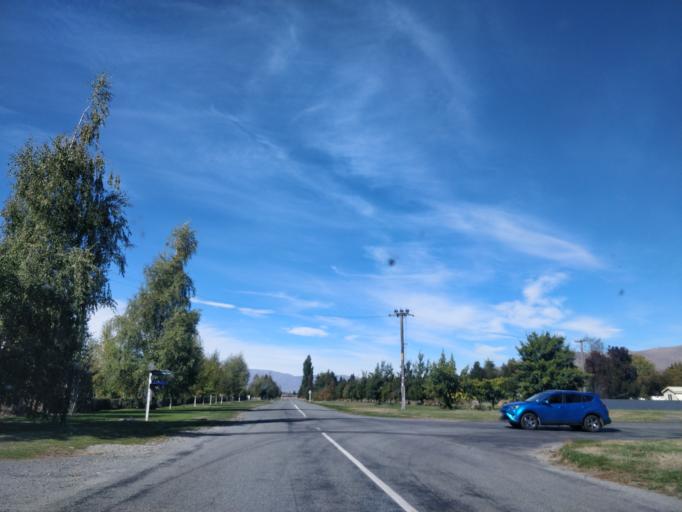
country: NZ
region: Canterbury
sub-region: Timaru District
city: Pleasant Point
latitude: -44.2527
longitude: 170.1017
